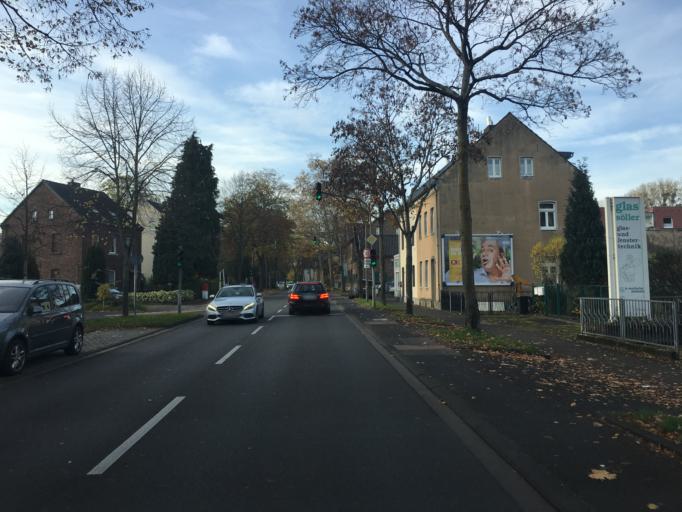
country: DE
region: North Rhine-Westphalia
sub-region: Regierungsbezirk Koln
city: Merheim
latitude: 50.9462
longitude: 7.0728
